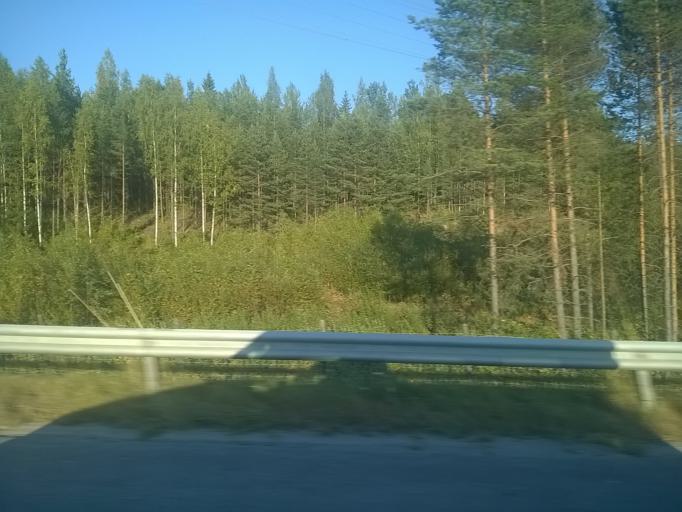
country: FI
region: Pirkanmaa
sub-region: Tampere
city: Tampere
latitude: 61.4295
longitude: 23.7547
